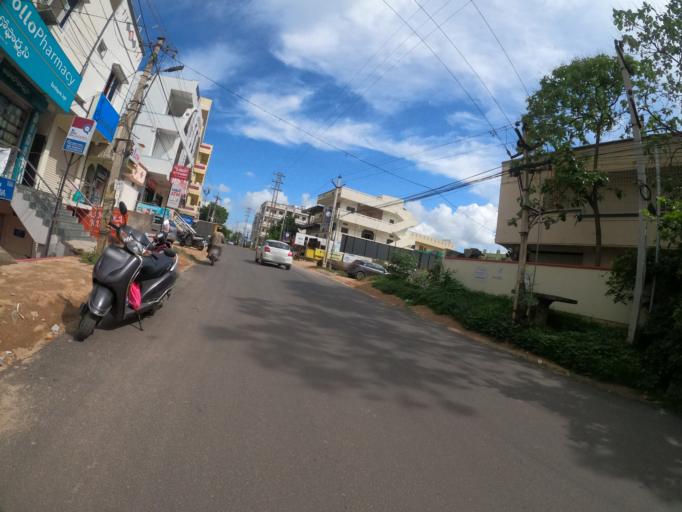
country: IN
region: Telangana
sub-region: Hyderabad
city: Hyderabad
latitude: 17.3531
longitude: 78.3893
